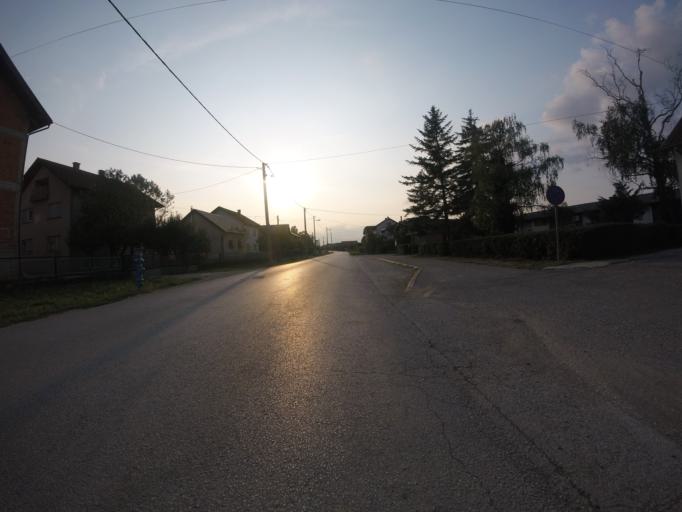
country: HR
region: Zagrebacka
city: Micevec
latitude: 45.7506
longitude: 16.1202
